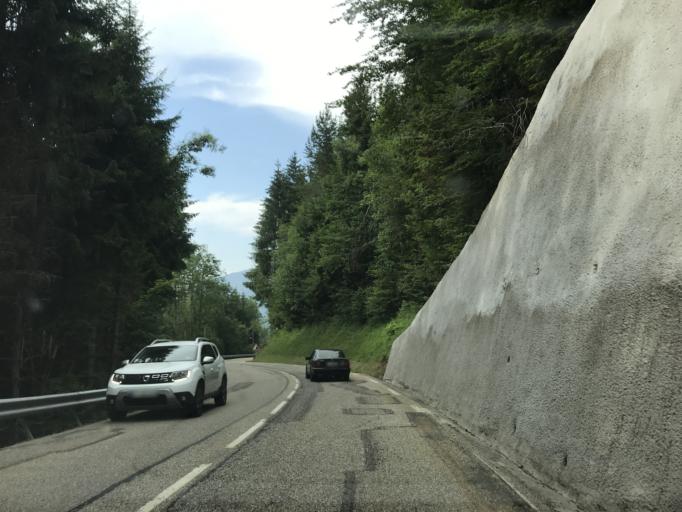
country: FR
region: Rhone-Alpes
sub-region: Departement de l'Isere
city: Allevard
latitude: 45.3383
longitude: 6.0935
